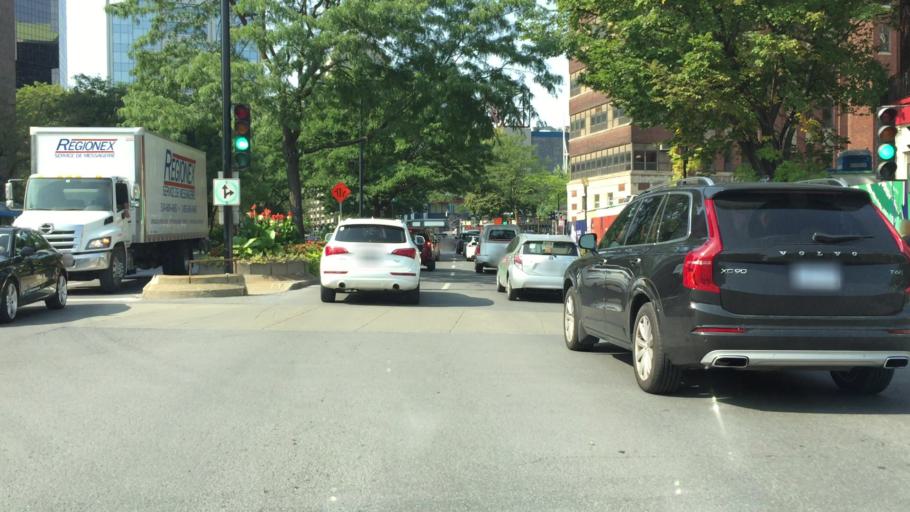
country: CA
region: Quebec
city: Westmount
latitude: 45.4881
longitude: -73.5830
